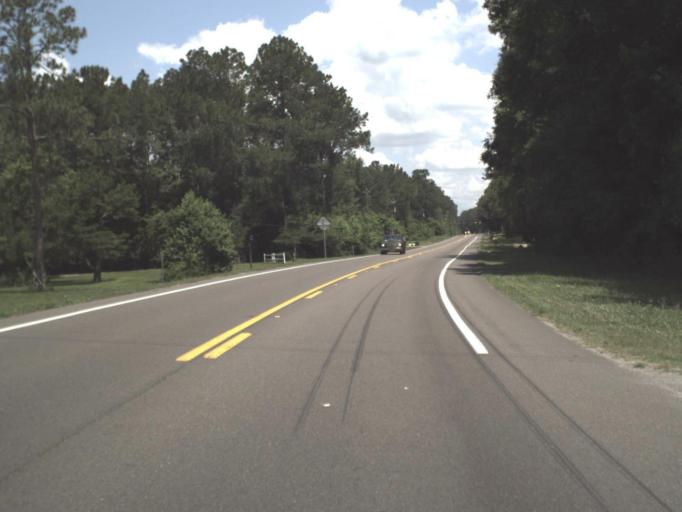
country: US
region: Florida
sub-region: Nassau County
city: Nassau Village-Ratliff
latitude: 30.5212
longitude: -81.7682
